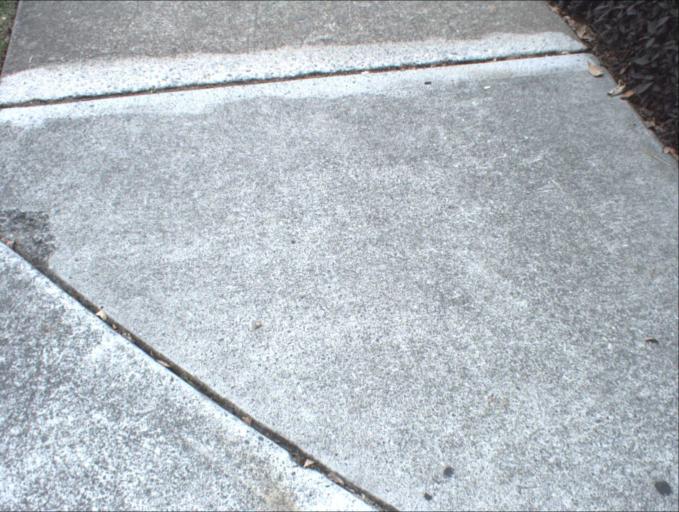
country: AU
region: Queensland
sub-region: Brisbane
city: Sunnybank Hills
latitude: -27.6641
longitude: 153.0430
